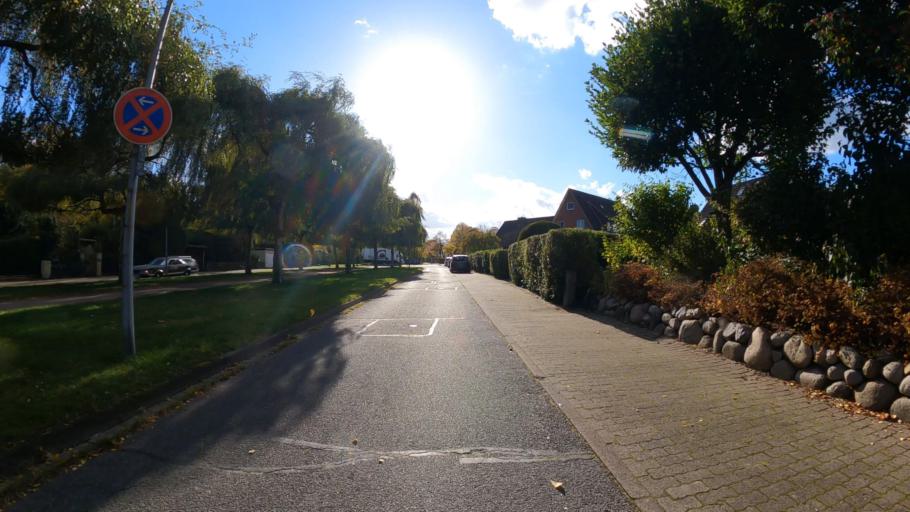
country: DE
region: Schleswig-Holstein
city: Ahrensburg
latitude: 53.6745
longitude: 10.2235
